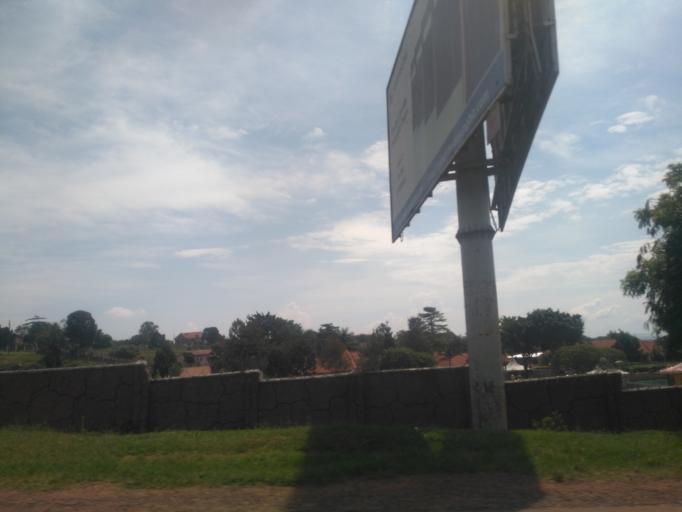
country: UG
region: Central Region
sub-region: Wakiso District
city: Entebbe
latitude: 0.0406
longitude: 32.4594
